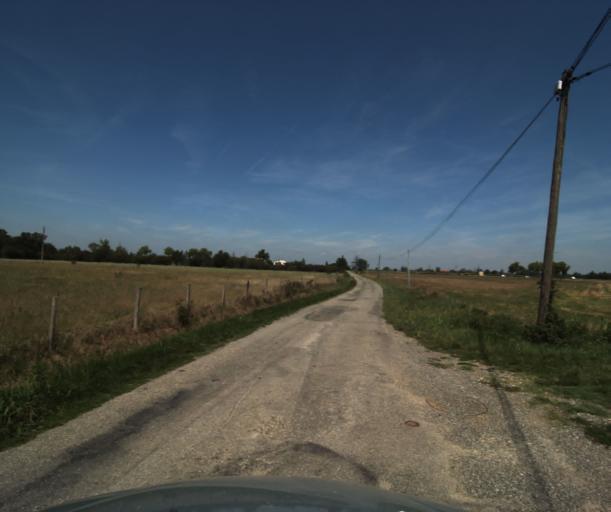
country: FR
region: Midi-Pyrenees
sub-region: Departement de la Haute-Garonne
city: Labastidette
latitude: 43.4630
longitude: 1.2686
